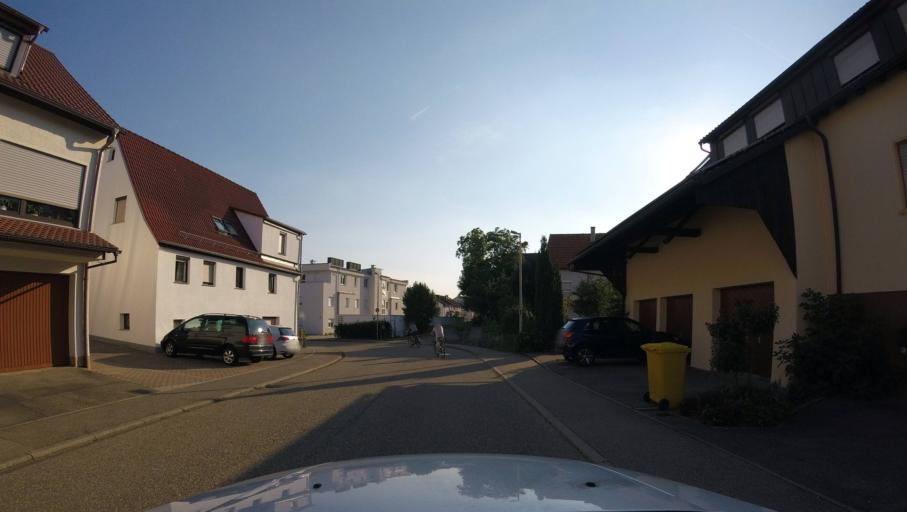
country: DE
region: Baden-Wuerttemberg
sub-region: Regierungsbezirk Stuttgart
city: Leutenbach
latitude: 48.9019
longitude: 9.4029
